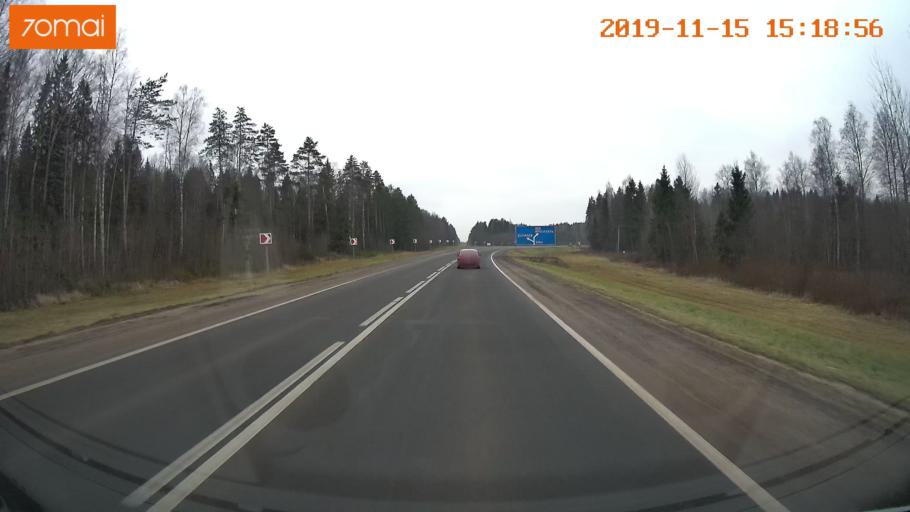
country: RU
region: Jaroslavl
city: Danilov
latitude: 58.2406
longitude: 40.1820
